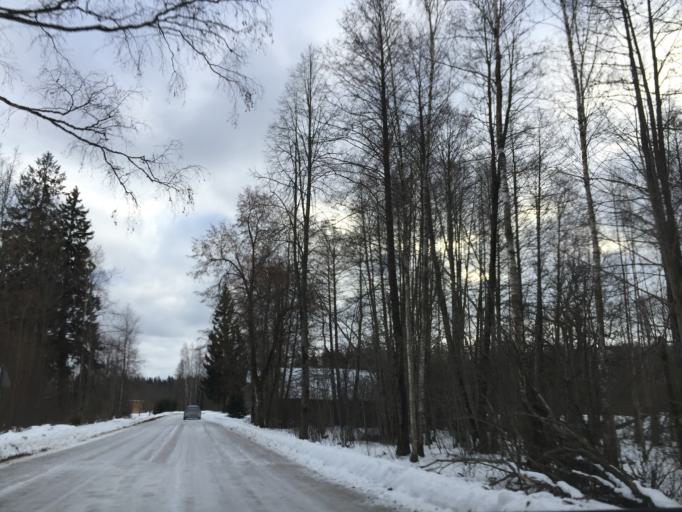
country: LV
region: Lielvarde
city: Lielvarde
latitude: 56.5789
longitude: 24.7886
